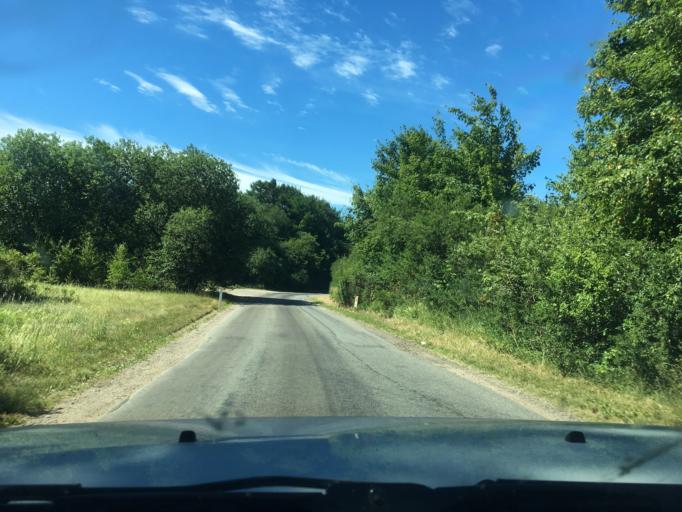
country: DK
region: Central Jutland
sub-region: Syddjurs Kommune
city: Ronde
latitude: 56.3375
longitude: 10.4231
